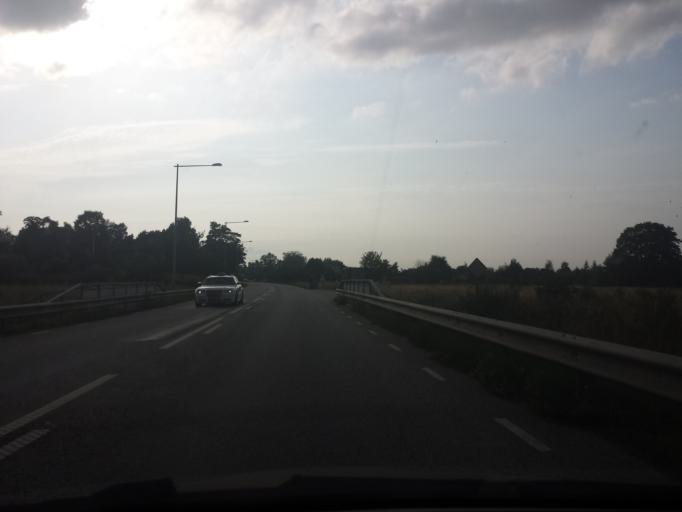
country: SE
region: Skane
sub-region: Ystads Kommun
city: Kopingebro
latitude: 55.4345
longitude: 13.9349
